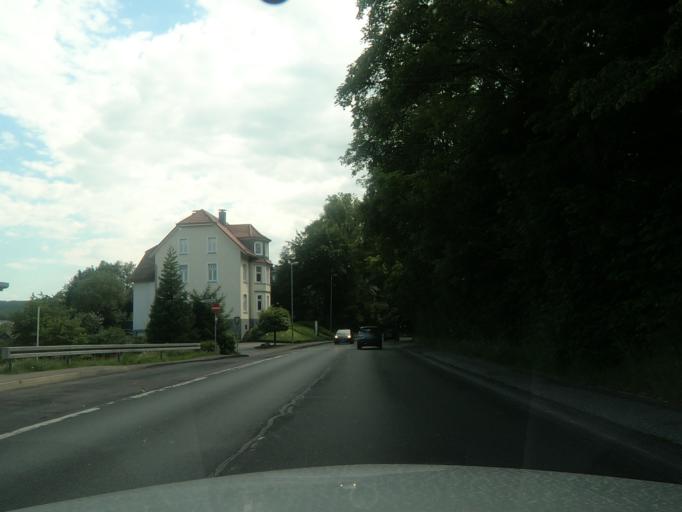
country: DE
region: North Rhine-Westphalia
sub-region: Regierungsbezirk Arnsberg
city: Olpe
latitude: 51.0351
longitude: 7.8549
